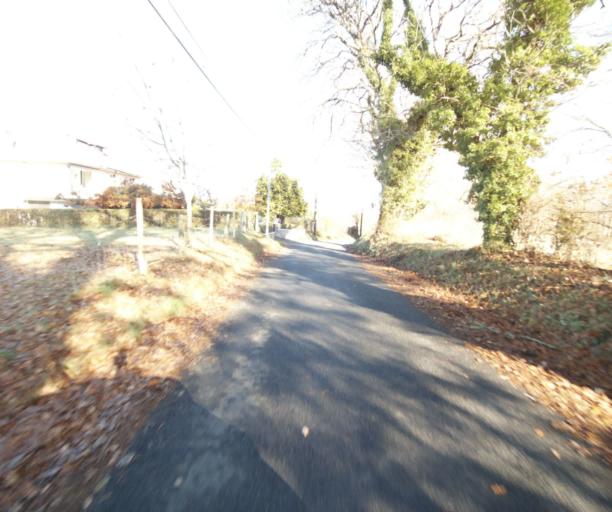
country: FR
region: Limousin
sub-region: Departement de la Correze
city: Laguenne
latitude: 45.2424
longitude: 1.7558
